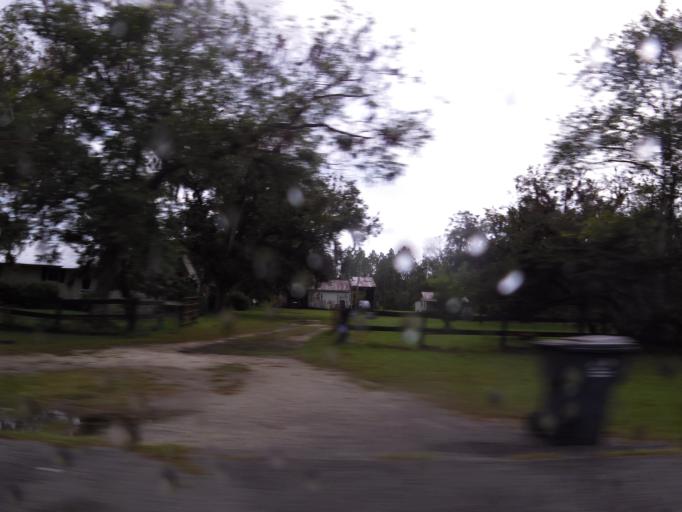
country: US
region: Florida
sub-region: Duval County
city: Baldwin
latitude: 30.4970
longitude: -82.0381
